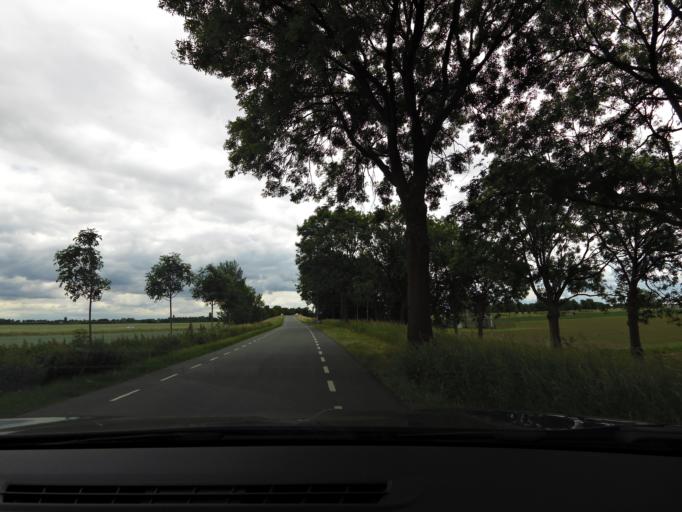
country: NL
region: South Holland
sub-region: Gemeente Oud-Beijerland
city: Oud-Beijerland
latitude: 51.7727
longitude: 4.4190
